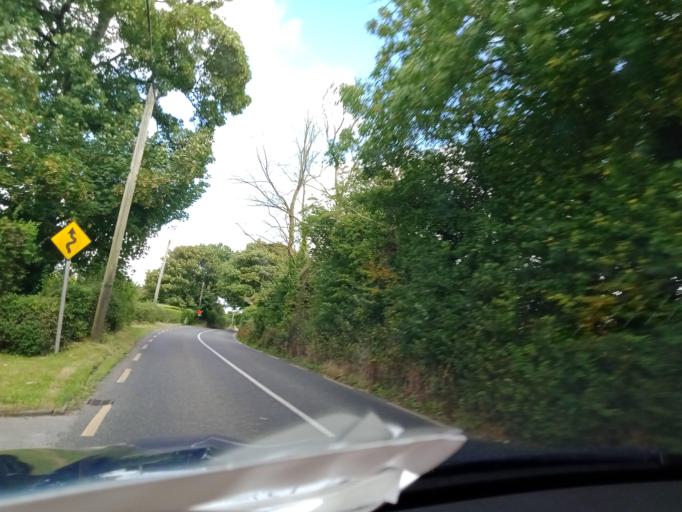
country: IE
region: Leinster
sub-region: Laois
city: Portlaoise
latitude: 53.0048
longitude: -7.2764
